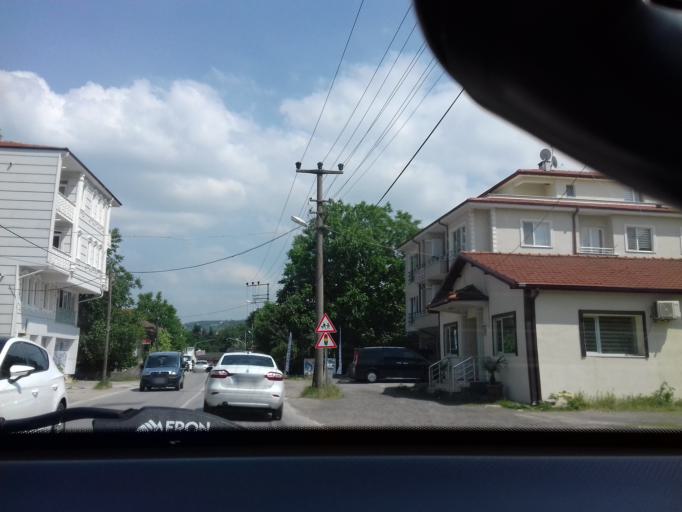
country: TR
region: Sakarya
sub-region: Merkez
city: Sapanca
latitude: 40.6880
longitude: 30.2660
